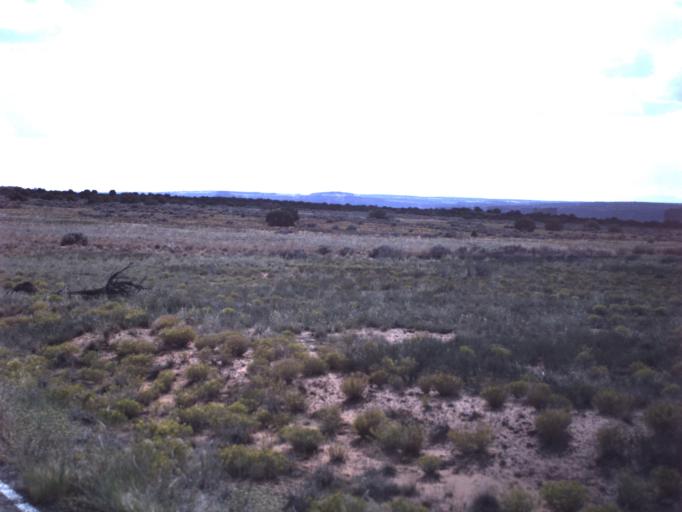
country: US
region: Utah
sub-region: Grand County
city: Moab
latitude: 38.5087
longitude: -109.7298
